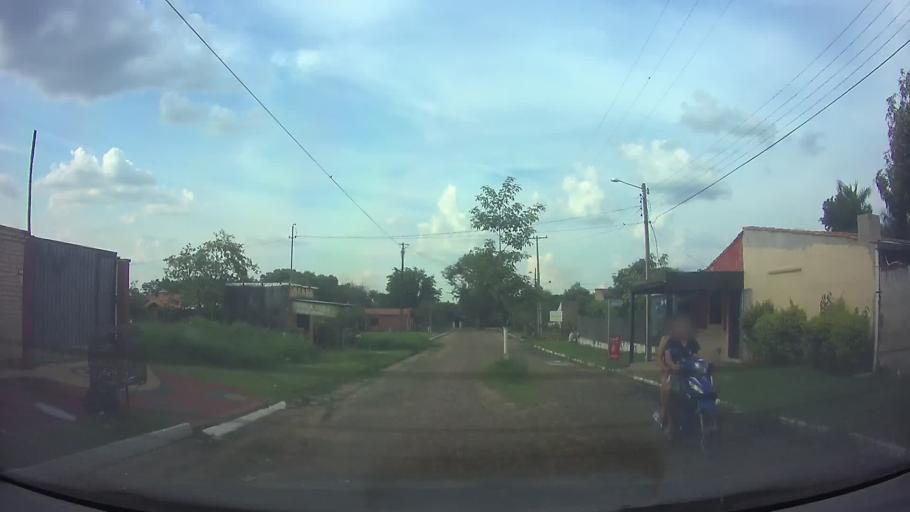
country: PY
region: Central
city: San Lorenzo
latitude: -25.2657
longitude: -57.4765
